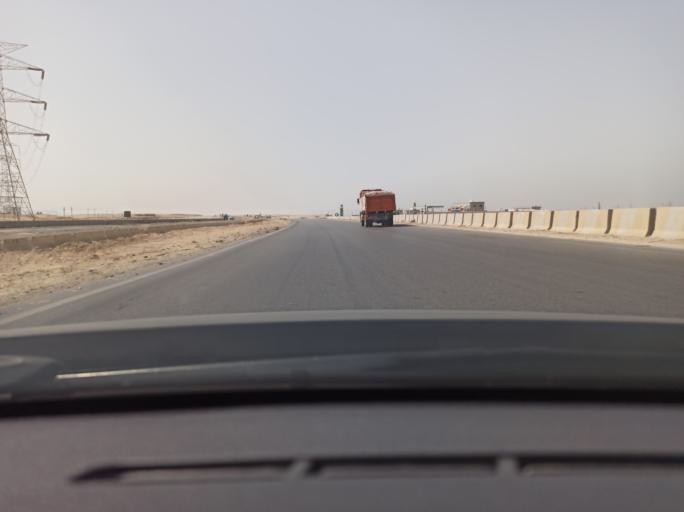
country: EG
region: Muhafazat al Fayyum
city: Al Wasitah
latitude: 29.3846
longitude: 31.3158
